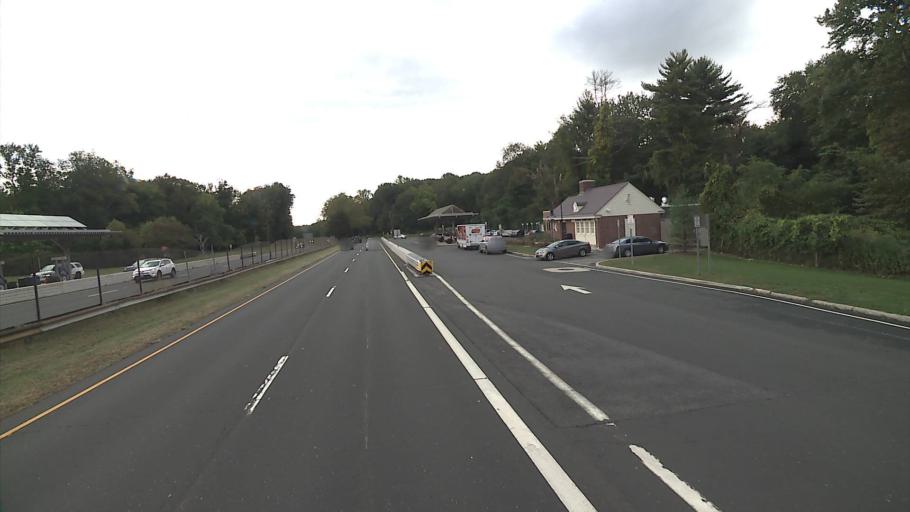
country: US
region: Connecticut
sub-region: Fairfield County
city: New Canaan
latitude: 41.1199
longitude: -73.4804
